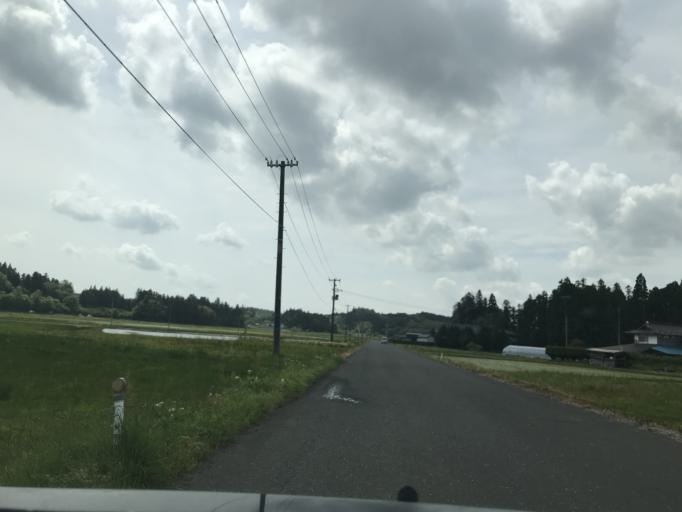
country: JP
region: Iwate
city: Ichinoseki
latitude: 38.8475
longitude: 141.0179
